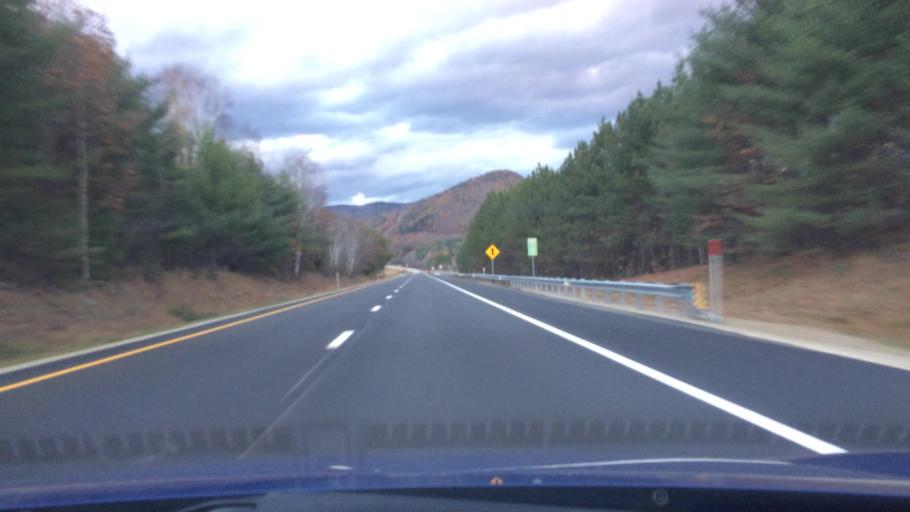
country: US
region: New Hampshire
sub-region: Grafton County
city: Woodstock
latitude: 43.9544
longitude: -71.6824
